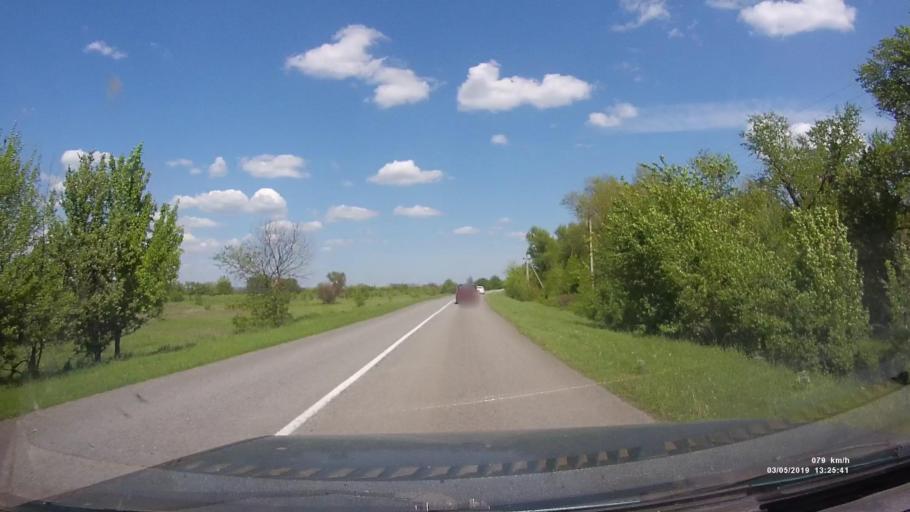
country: RU
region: Rostov
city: Semikarakorsk
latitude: 47.5683
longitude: 40.8071
